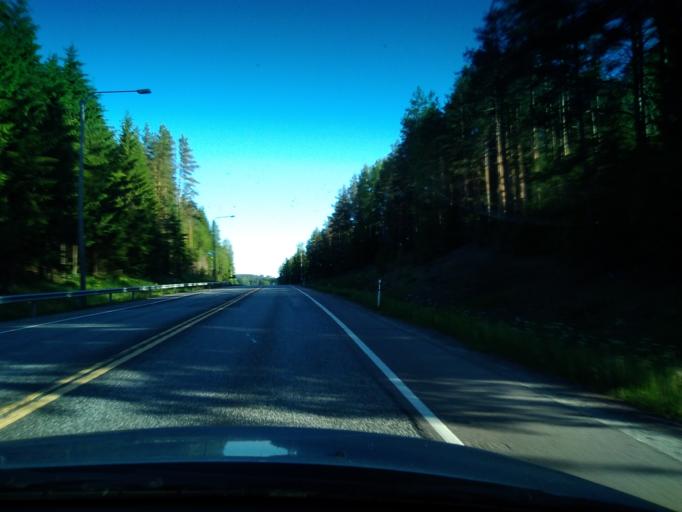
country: FI
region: Uusimaa
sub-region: Helsinki
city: Karkkila
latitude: 60.5582
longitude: 24.1986
